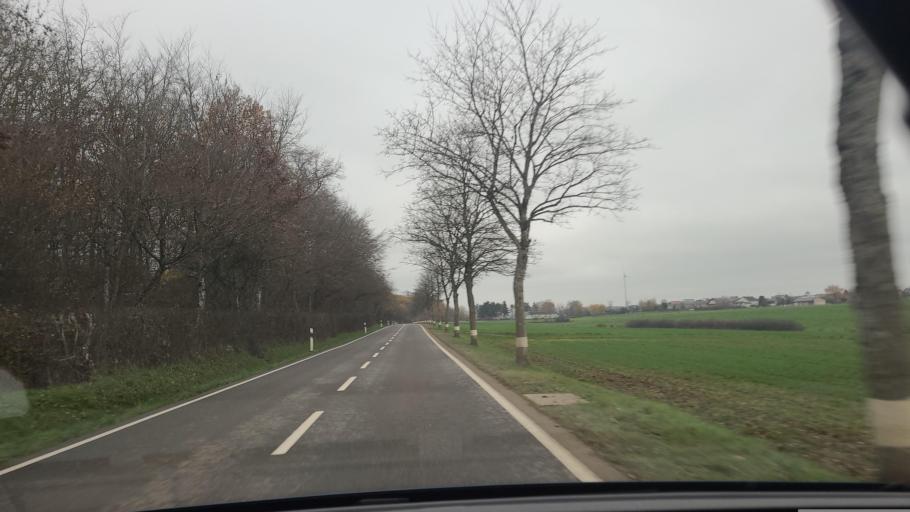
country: LU
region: Luxembourg
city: Schouweiler
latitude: 49.5913
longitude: 5.9481
